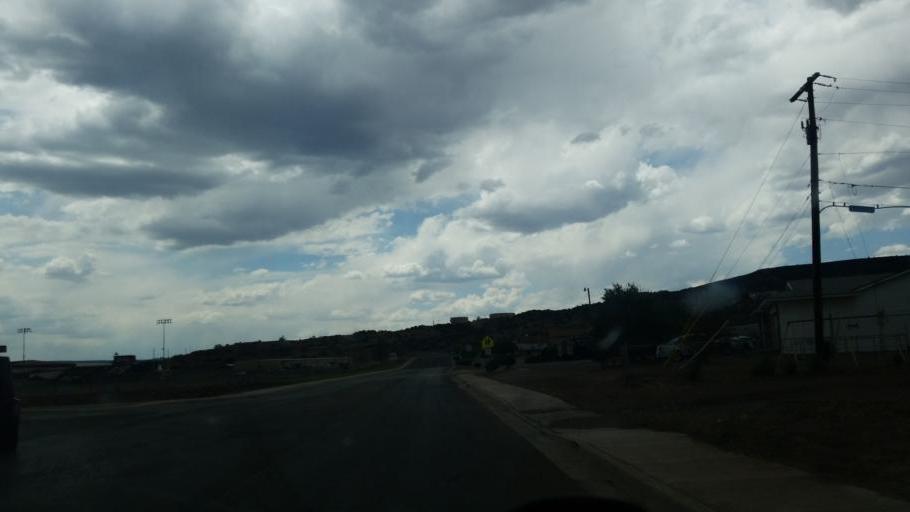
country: US
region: New Mexico
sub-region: Cibola County
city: Grants
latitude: 35.1611
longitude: -107.8426
